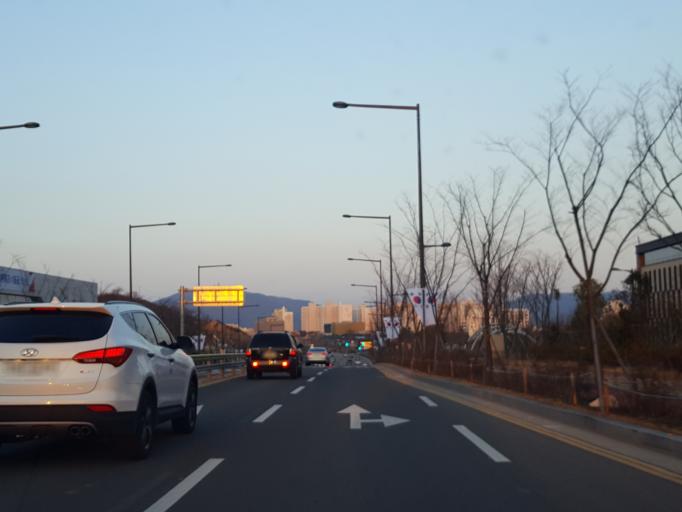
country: KR
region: Ulsan
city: Ulsan
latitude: 35.5655
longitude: 129.3188
